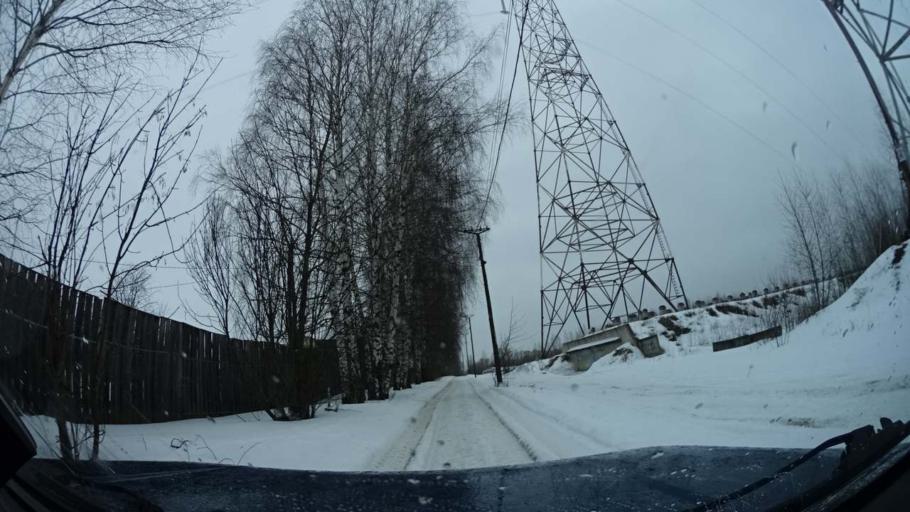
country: RU
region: Tverskaya
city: Konakovo
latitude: 56.7274
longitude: 36.7733
